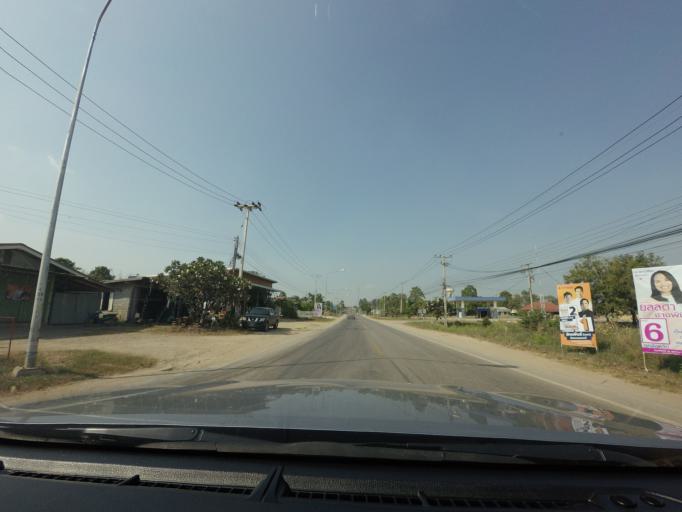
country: TH
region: Phitsanulok
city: Bang Rakam
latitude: 16.7965
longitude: 100.0300
